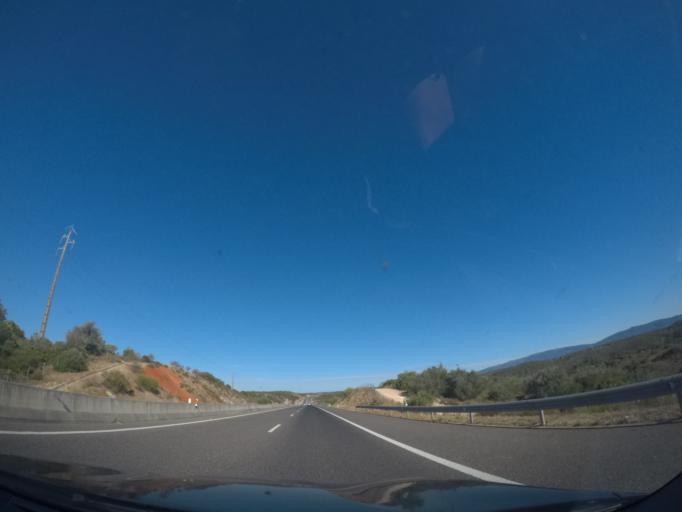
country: PT
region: Faro
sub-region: Lagoa
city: Estombar
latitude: 37.1595
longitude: -8.4959
